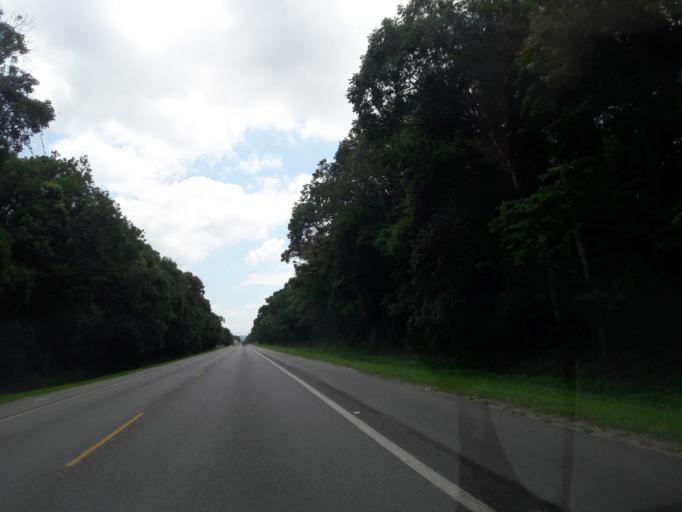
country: BR
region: Parana
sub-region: Pontal Do Parana
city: Pontal do Parana
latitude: -25.6024
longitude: -48.5569
